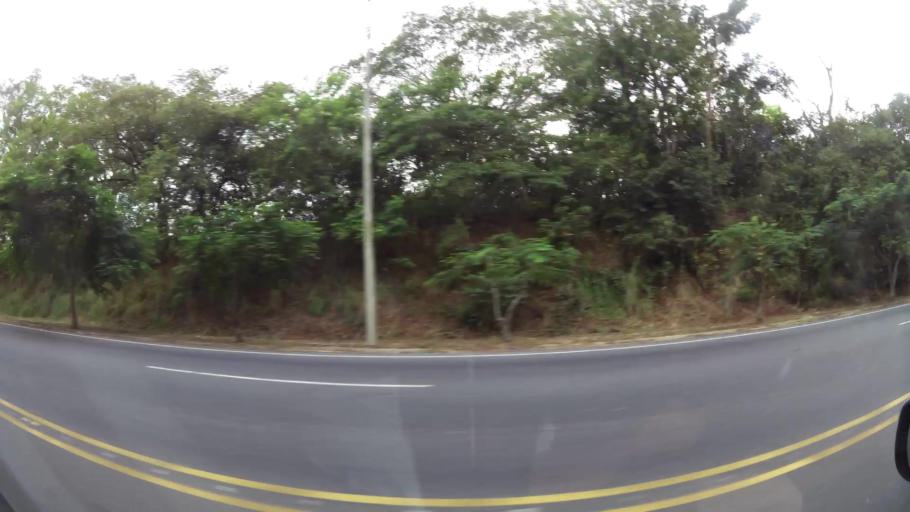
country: CR
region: Puntarenas
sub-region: Canton Central de Puntarenas
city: Chacarita
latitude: 9.9520
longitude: -84.7313
